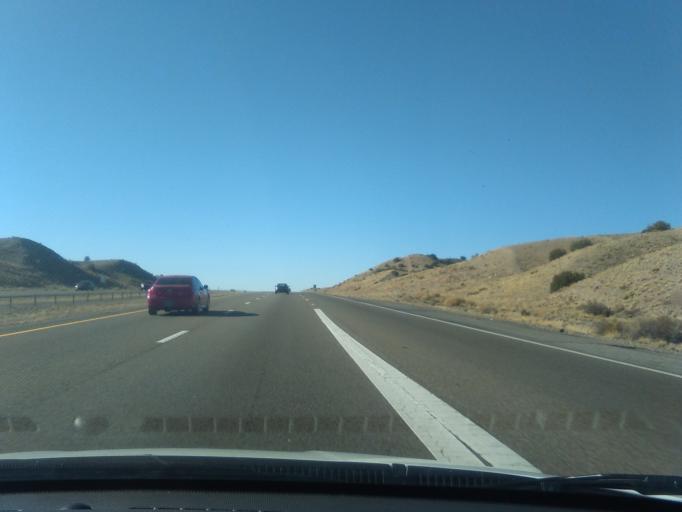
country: US
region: New Mexico
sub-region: Sandoval County
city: San Felipe Pueblo
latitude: 35.4153
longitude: -106.4100
